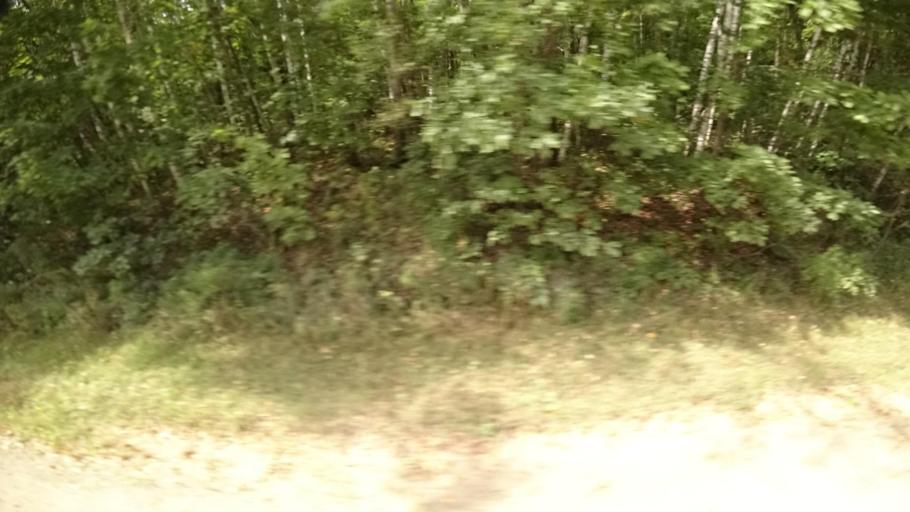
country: RU
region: Primorskiy
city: Yakovlevka
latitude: 44.6710
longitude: 133.6113
